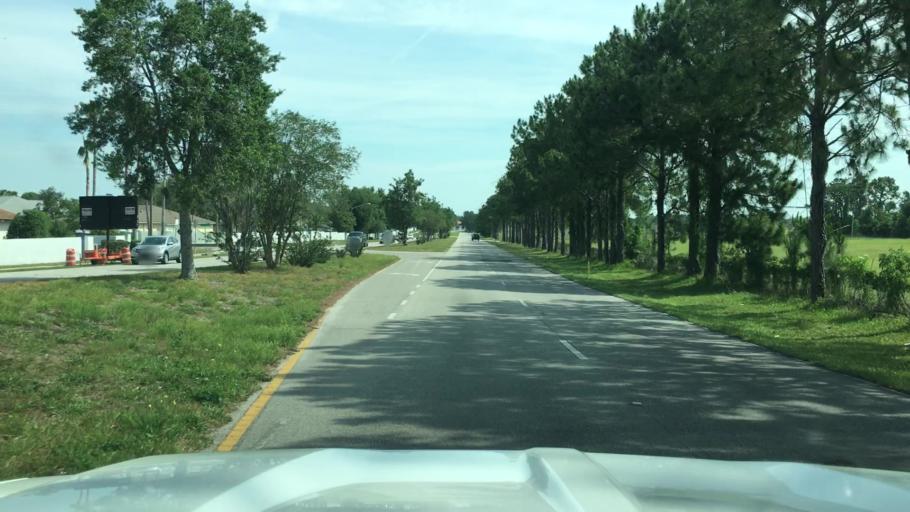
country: US
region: Florida
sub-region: Pasco County
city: Shady Hills
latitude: 28.4434
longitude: -82.5421
